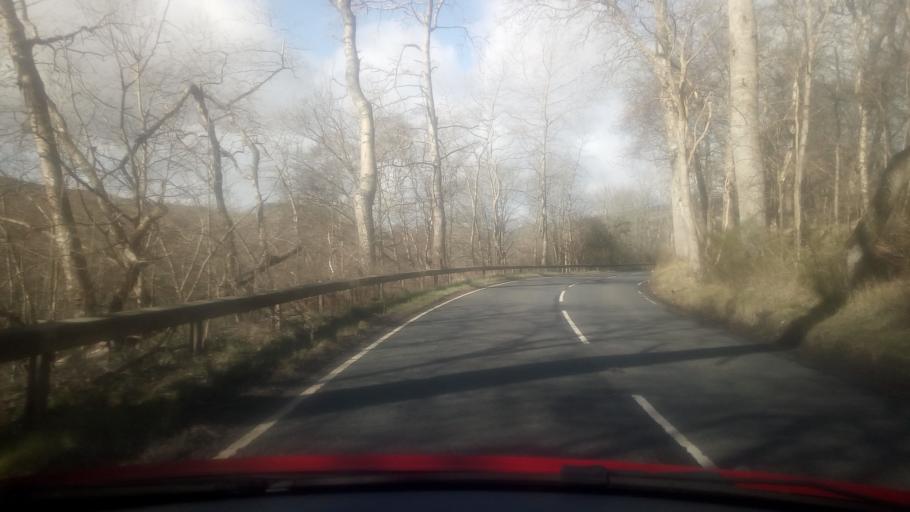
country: GB
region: Scotland
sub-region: The Scottish Borders
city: Selkirk
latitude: 55.6093
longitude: -2.9053
